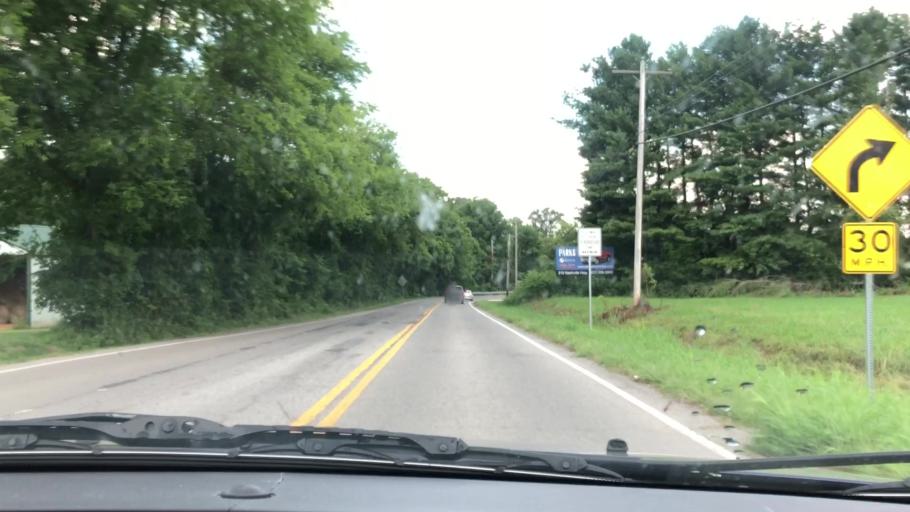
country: US
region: Tennessee
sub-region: Maury County
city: Columbia
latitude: 35.6710
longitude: -87.0052
